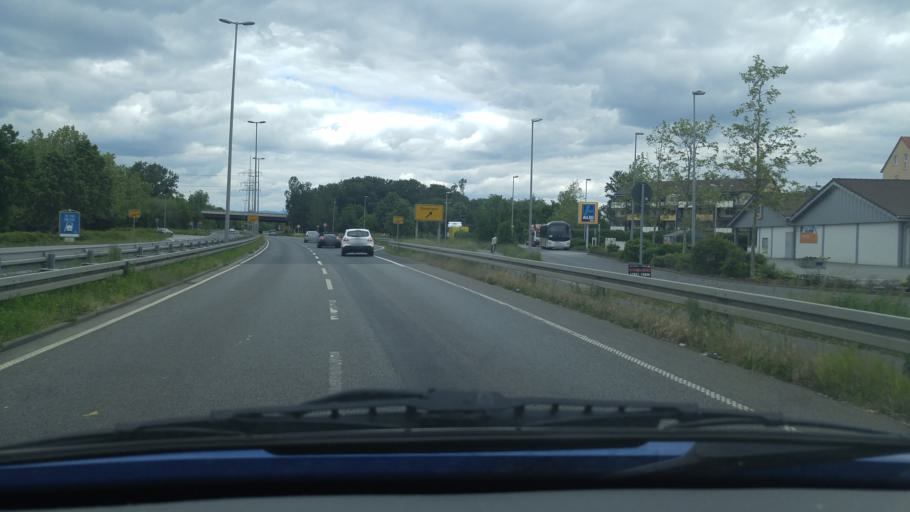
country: DE
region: Hesse
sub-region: Regierungsbezirk Darmstadt
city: Florsheim
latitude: 50.0014
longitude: 8.4256
